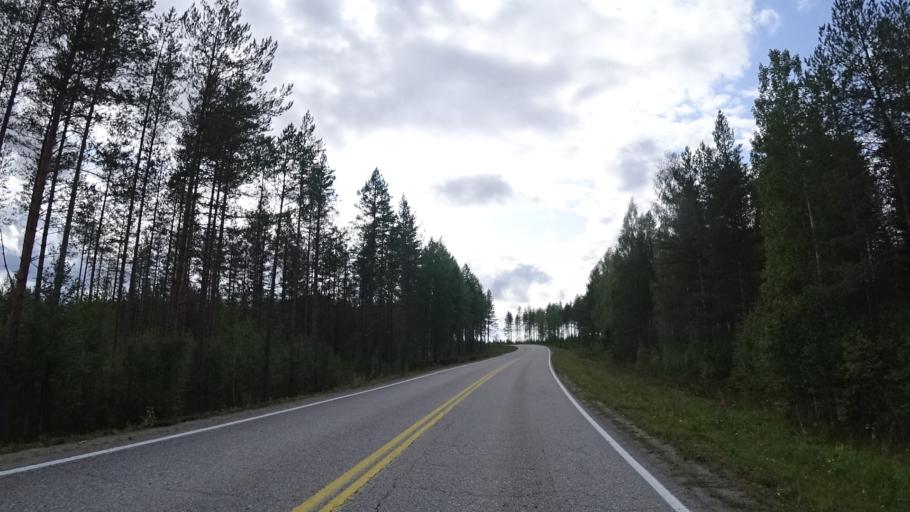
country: FI
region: North Karelia
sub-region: Joensuu
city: Ilomantsi
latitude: 62.7793
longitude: 31.0790
